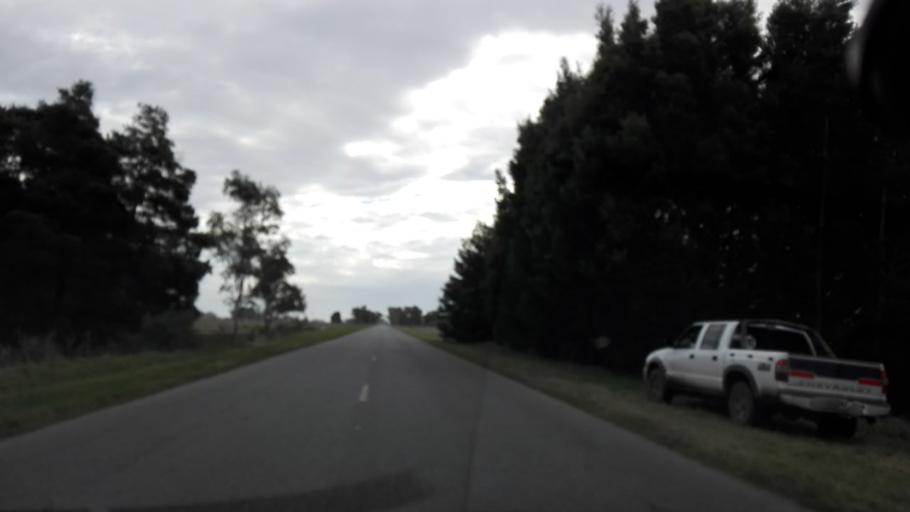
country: AR
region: Buenos Aires
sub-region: Partido de Las Flores
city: Las Flores
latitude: -36.2048
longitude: -59.0497
